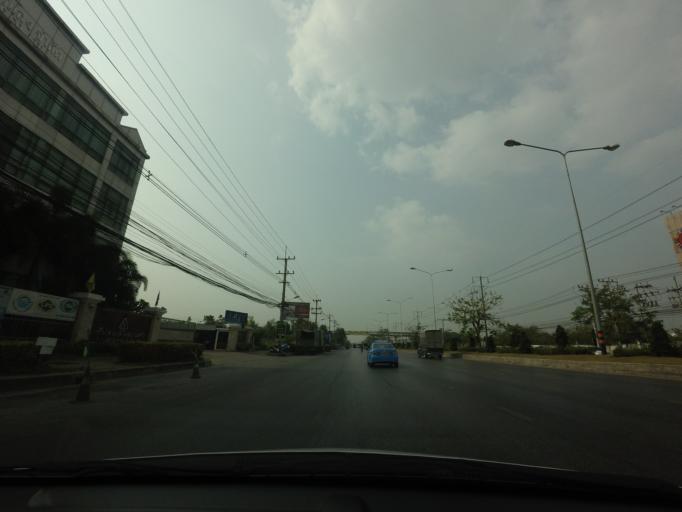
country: TH
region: Bangkok
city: Nong Khaem
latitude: 13.7357
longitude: 100.3297
